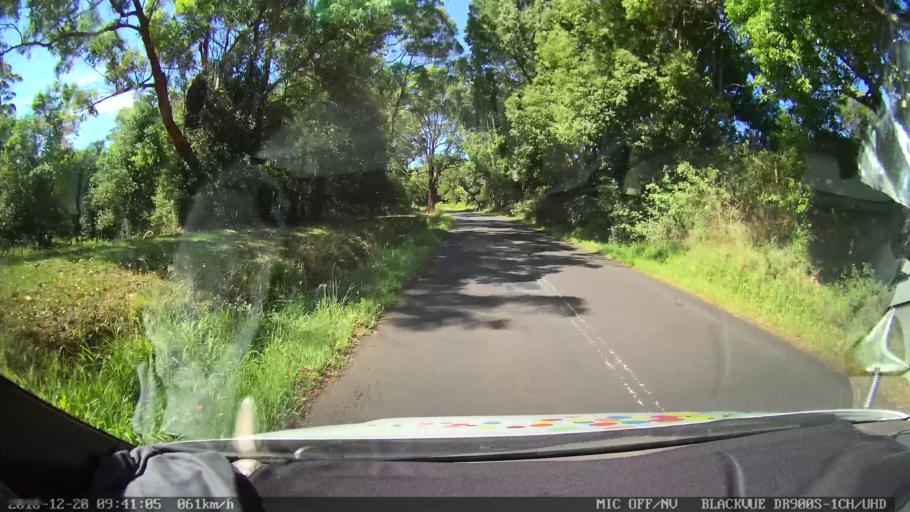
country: AU
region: New South Wales
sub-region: Lismore Municipality
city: Lismore
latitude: -28.7063
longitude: 153.3018
